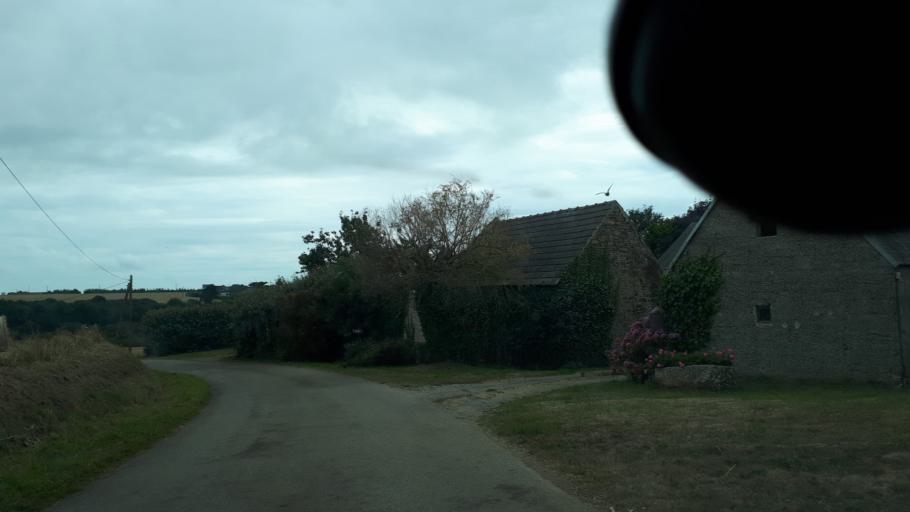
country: FR
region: Brittany
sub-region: Departement du Finistere
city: Plozevet
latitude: 47.9671
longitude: -4.3945
